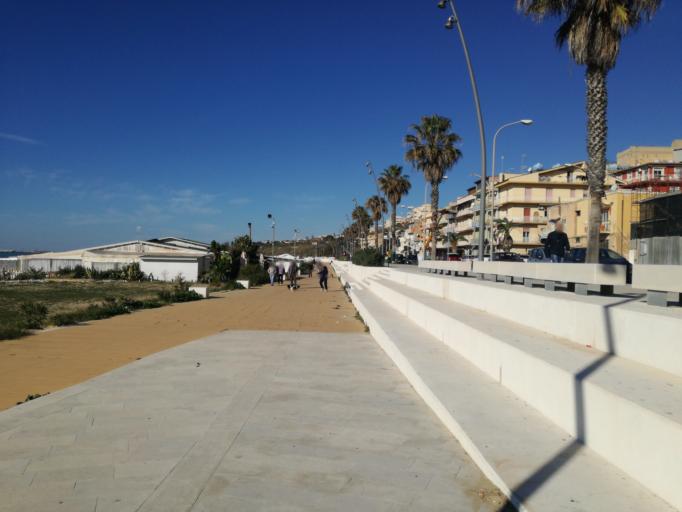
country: IT
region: Sicily
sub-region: Provincia di Caltanissetta
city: Gela
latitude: 37.0649
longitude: 14.2459
